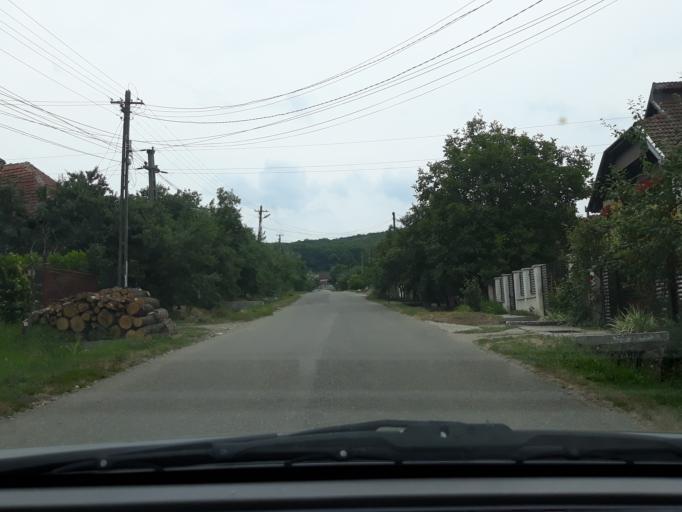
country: RO
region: Salaj
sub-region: Comuna Criseni
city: Criseni
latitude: 47.2518
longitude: 23.0674
